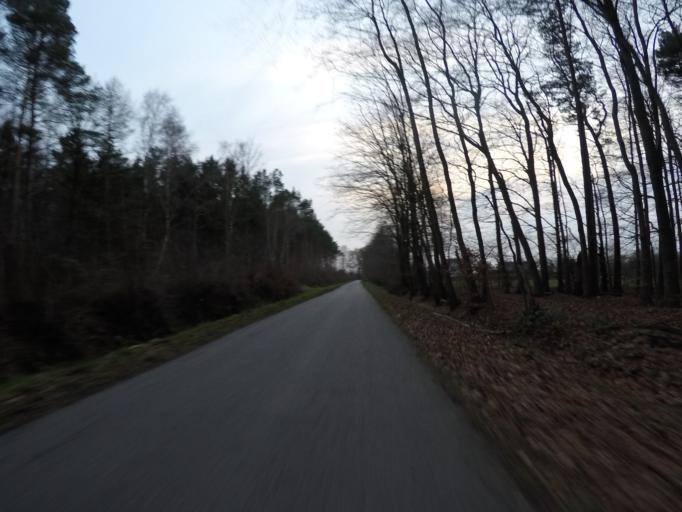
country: DE
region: Schleswig-Holstein
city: Bilsen
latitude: 53.7301
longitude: 9.8660
